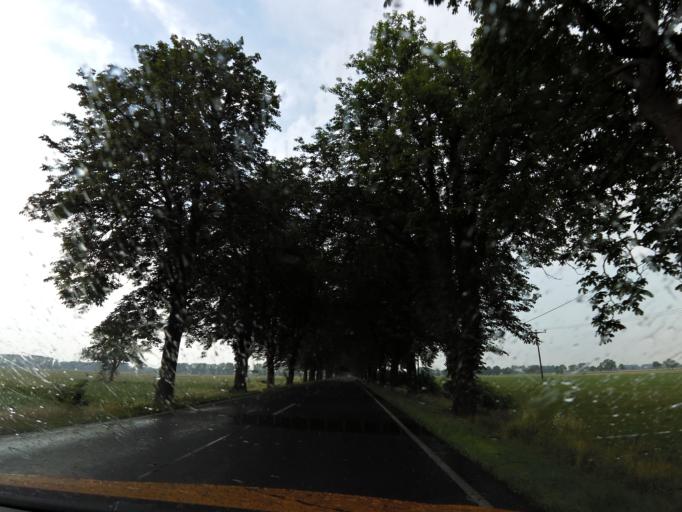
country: DE
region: Brandenburg
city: Friesack
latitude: 52.7537
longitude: 12.5719
